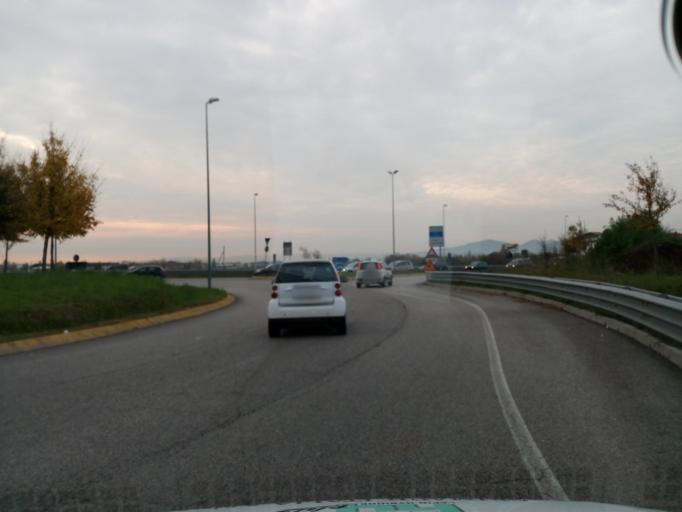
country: IT
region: Veneto
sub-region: Provincia di Vicenza
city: Thiene
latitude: 45.6977
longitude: 11.4599
